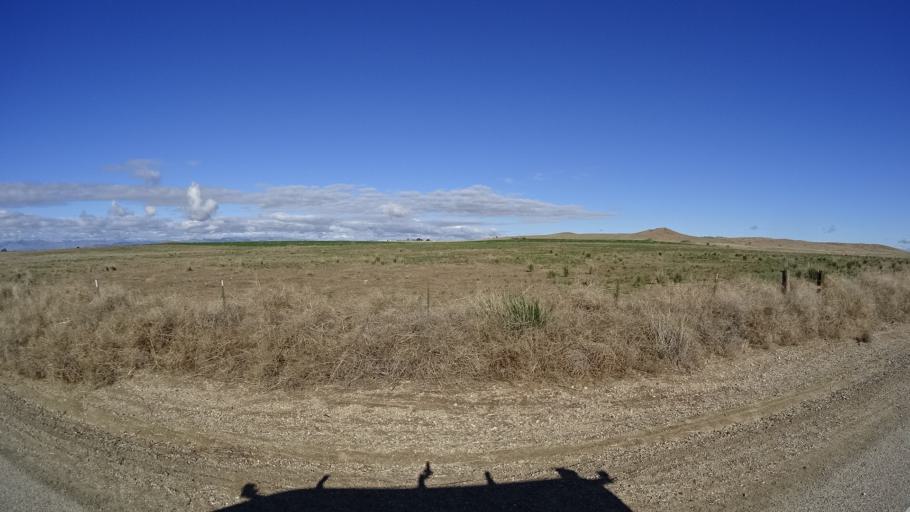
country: US
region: Idaho
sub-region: Ada County
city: Kuna
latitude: 43.4262
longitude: -116.4139
